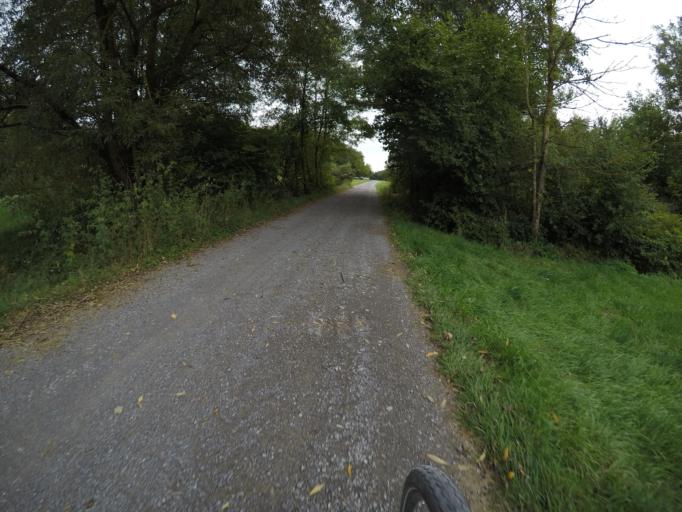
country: DE
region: Baden-Wuerttemberg
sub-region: Karlsruhe Region
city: Illingen
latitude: 48.9686
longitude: 8.8888
